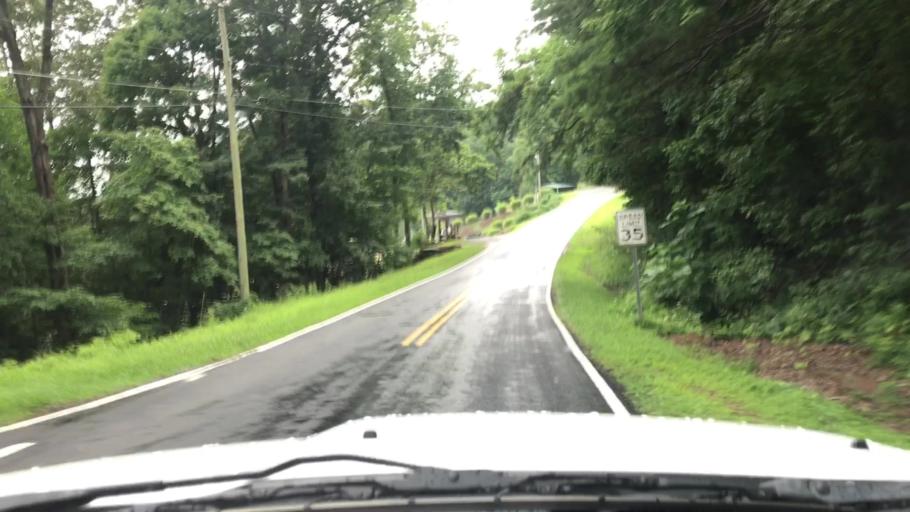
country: US
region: North Carolina
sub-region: Graham County
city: Robbinsville
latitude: 35.3665
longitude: -83.8564
